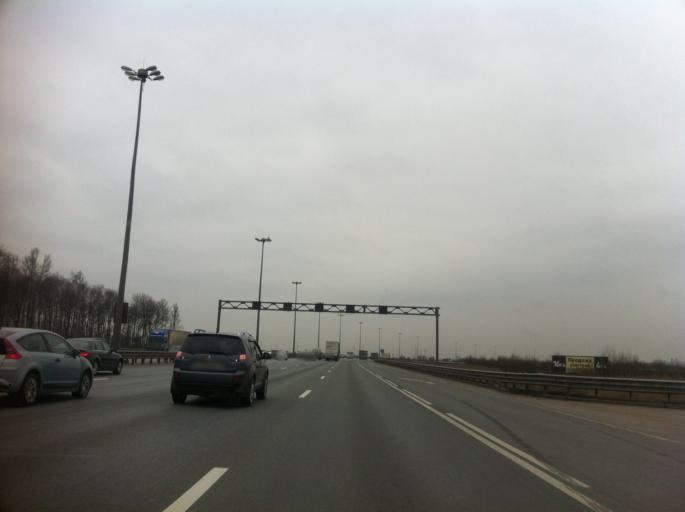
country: RU
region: Leningrad
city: Rybatskoye
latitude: 59.8758
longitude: 30.5304
